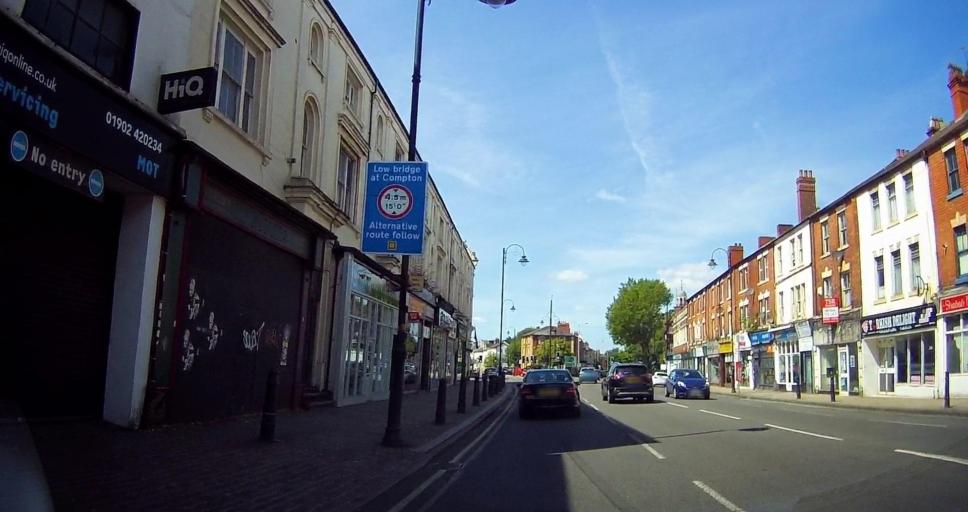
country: GB
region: England
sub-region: Wolverhampton
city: Wolverhampton
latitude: 52.5850
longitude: -2.1386
